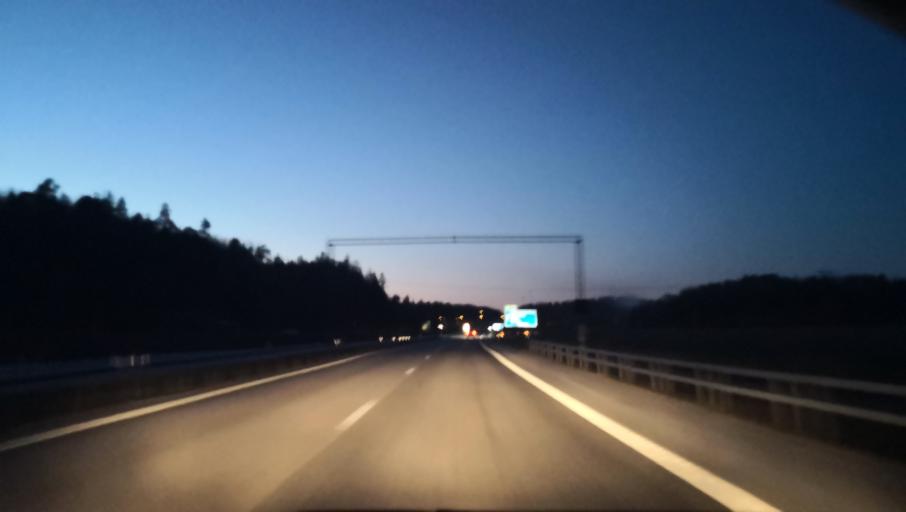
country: SE
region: Stockholm
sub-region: Nynashamns Kommun
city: Osmo
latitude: 58.9681
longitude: 17.9080
